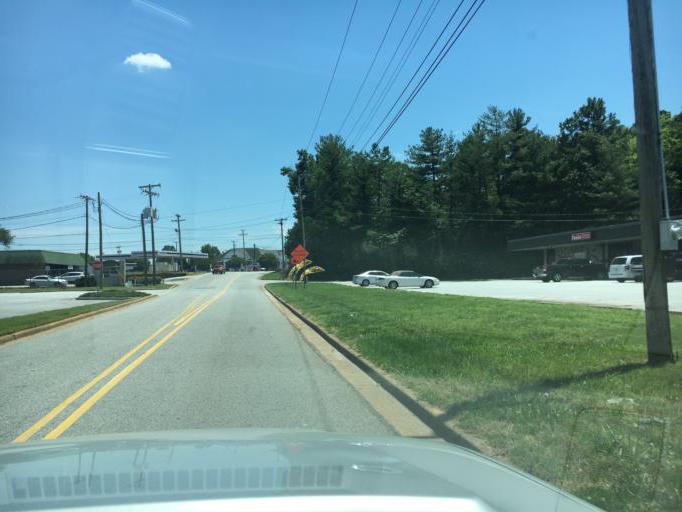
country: US
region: South Carolina
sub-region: Greenville County
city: Greer
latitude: 34.9437
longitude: -82.2489
